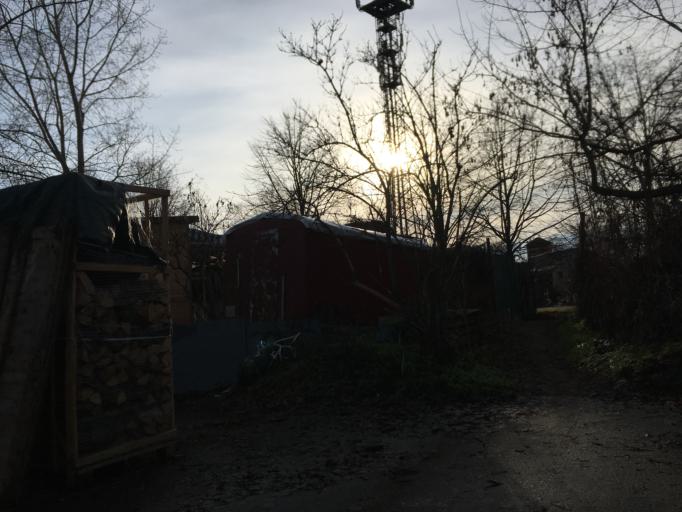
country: DE
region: Berlin
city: Blankenburg
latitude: 52.6147
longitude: 13.4528
